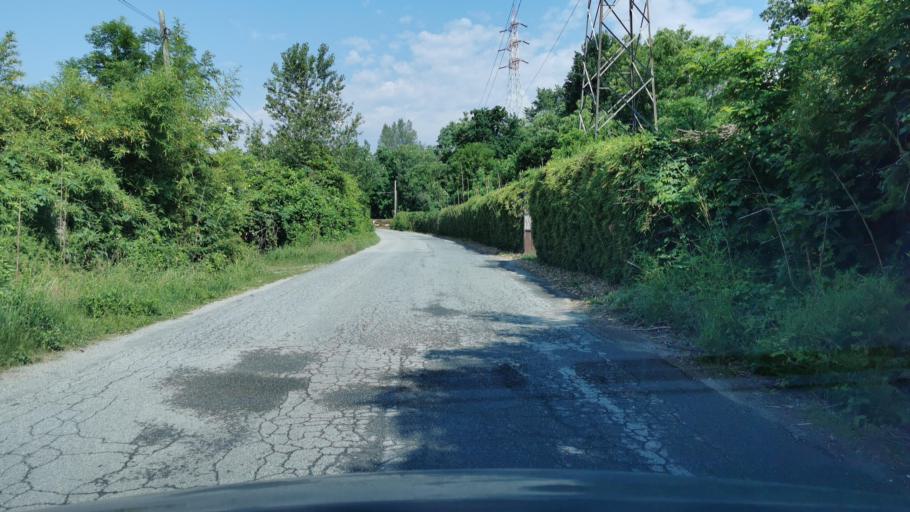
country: IT
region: Piedmont
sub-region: Provincia di Torino
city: Villanova Canavese
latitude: 45.2418
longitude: 7.5485
